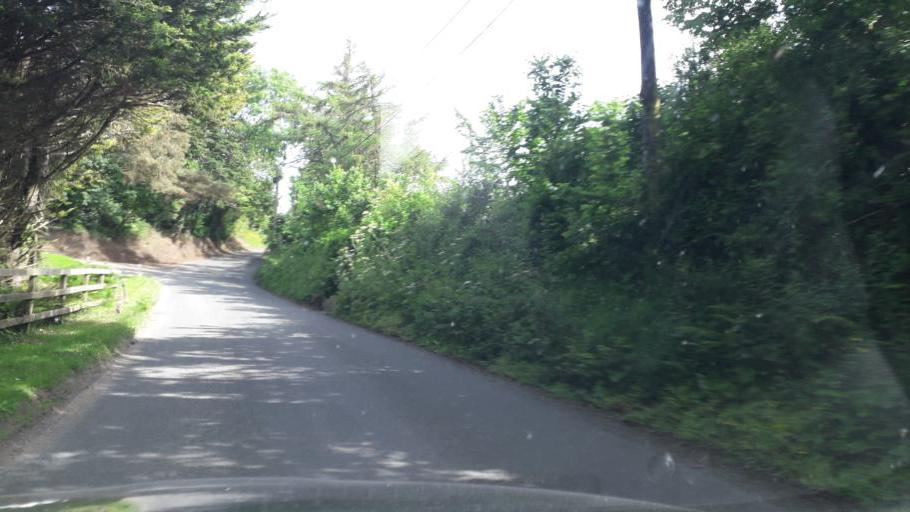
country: IE
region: Leinster
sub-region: Loch Garman
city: Castlebridge
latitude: 52.4052
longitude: -6.4062
